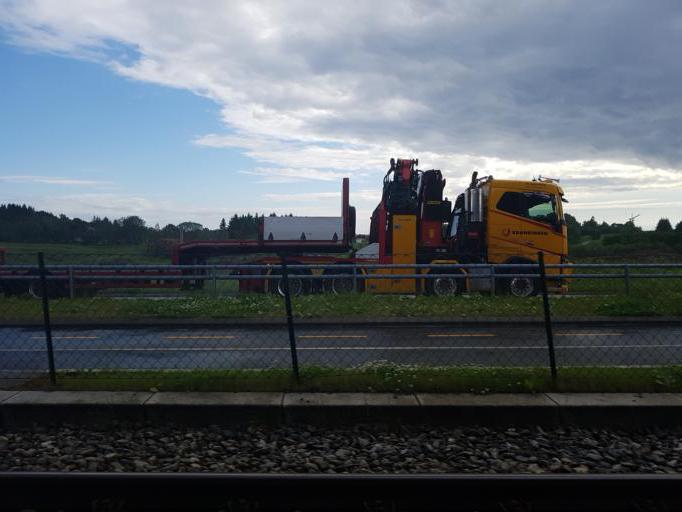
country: NO
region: Hordaland
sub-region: Bergen
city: Ytrebygda
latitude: 60.2914
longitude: 5.2482
